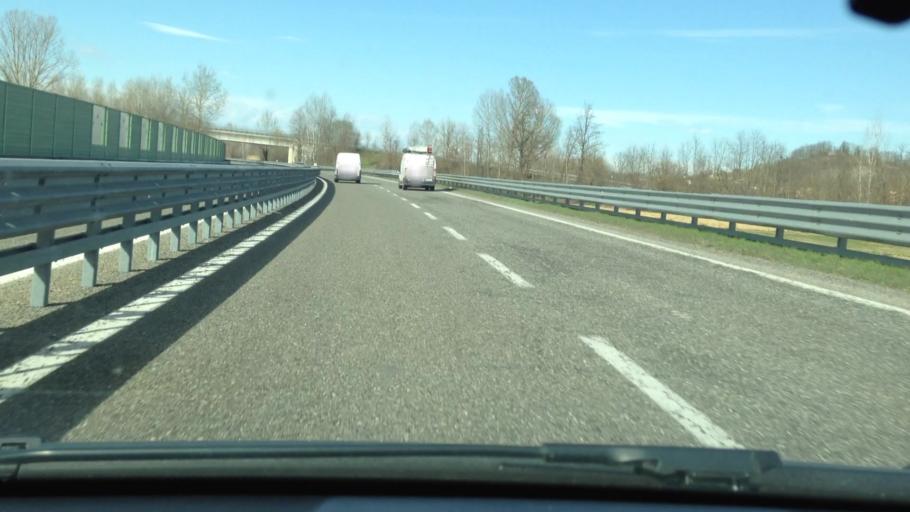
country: IT
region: Piedmont
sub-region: Provincia di Asti
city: Portacomaro
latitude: 44.9425
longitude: 8.2257
